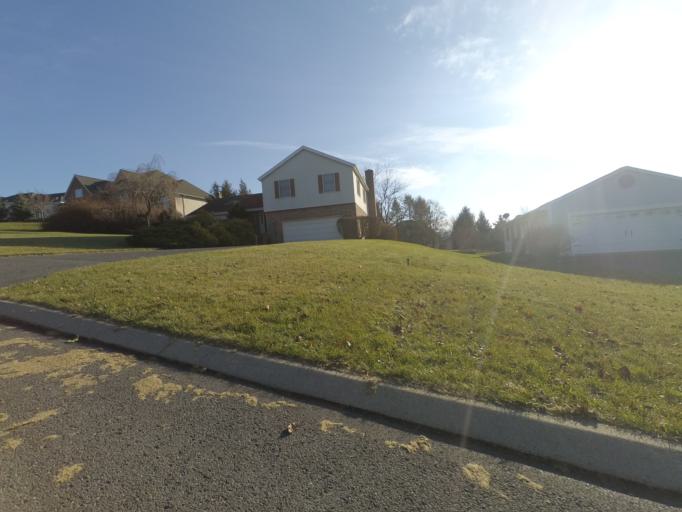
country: US
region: Pennsylvania
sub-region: Centre County
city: Lemont
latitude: 40.7964
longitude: -77.8249
